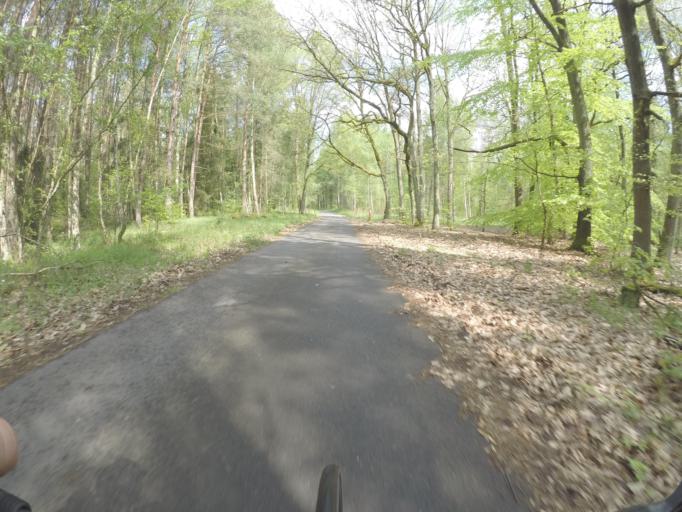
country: DE
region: Brandenburg
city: Marienwerder
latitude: 52.8713
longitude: 13.6162
